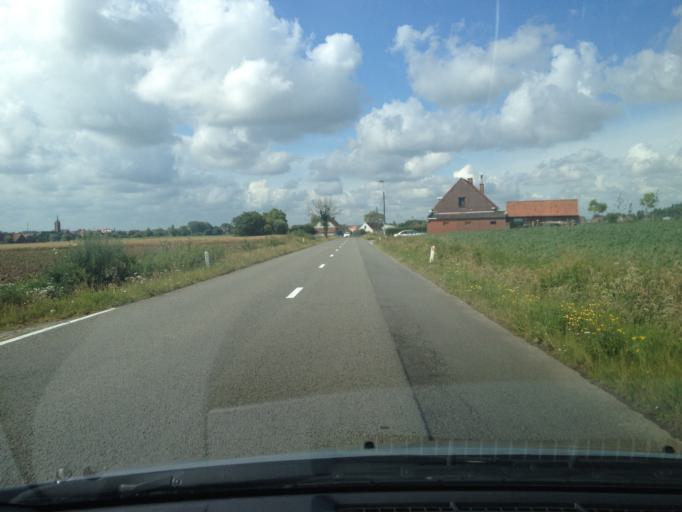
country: FR
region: Nord-Pas-de-Calais
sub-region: Departement du Nord
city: Hondschoote
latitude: 50.9319
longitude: 2.6272
